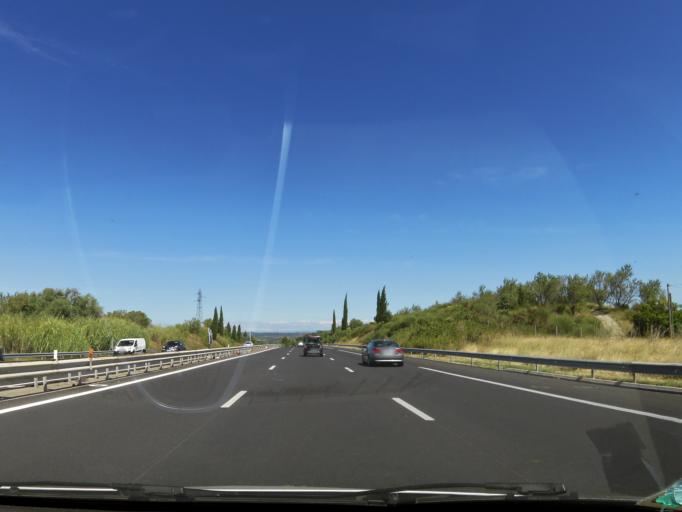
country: FR
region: Languedoc-Roussillon
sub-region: Departement du Gard
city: Sernhac
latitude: 43.9032
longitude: 4.5446
